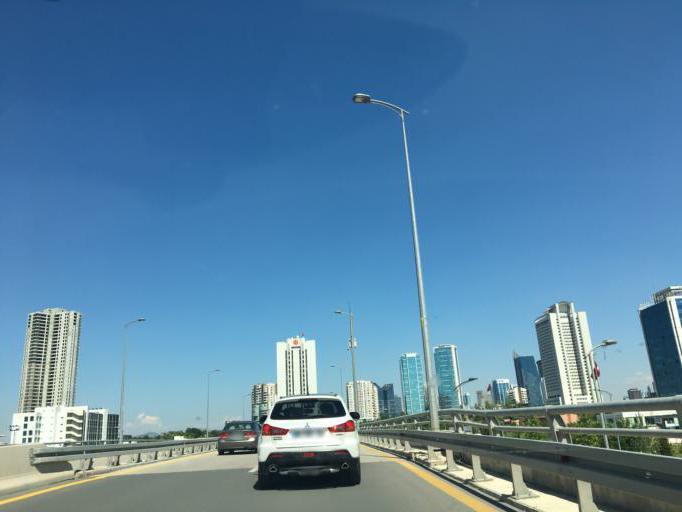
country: TR
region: Ankara
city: Ankara
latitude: 39.9133
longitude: 32.7852
